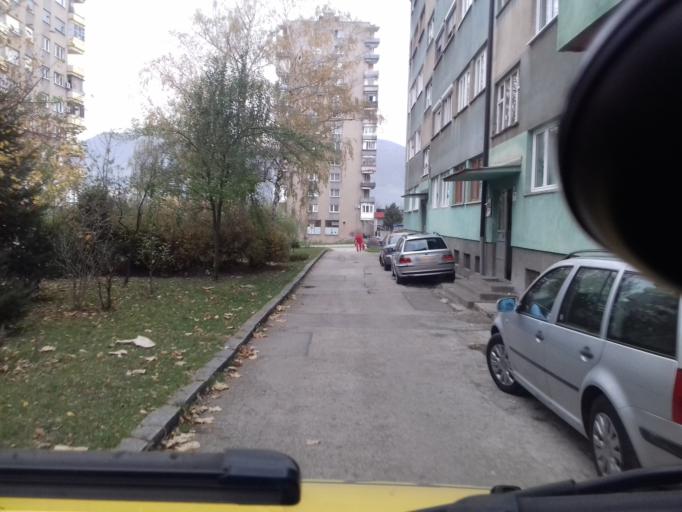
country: BA
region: Federation of Bosnia and Herzegovina
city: Zenica
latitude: 44.2043
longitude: 17.9223
